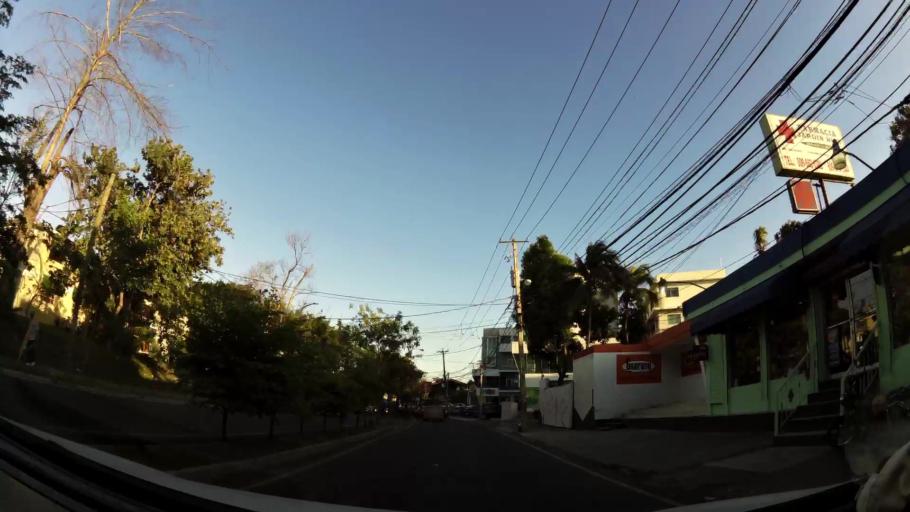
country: DO
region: Nacional
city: La Agustina
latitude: 18.4845
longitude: -69.9599
